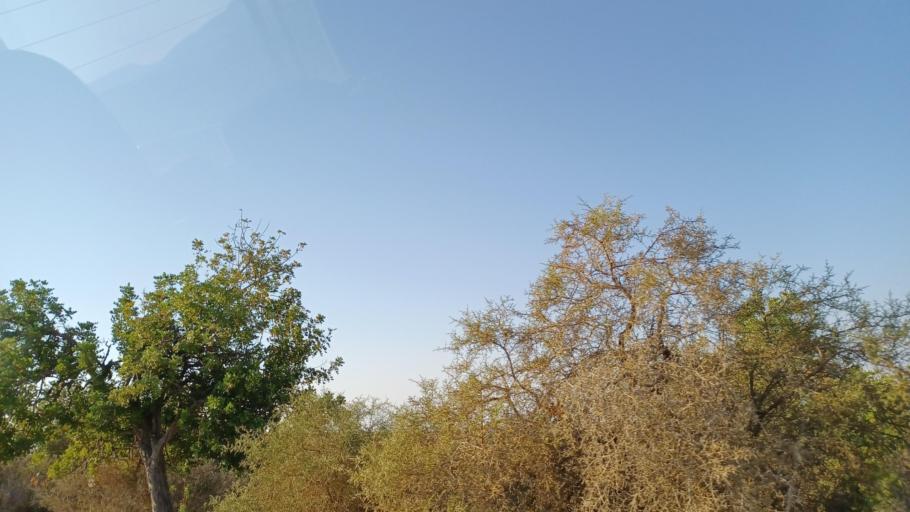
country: CY
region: Limassol
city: Pissouri
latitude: 34.7284
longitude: 32.6744
